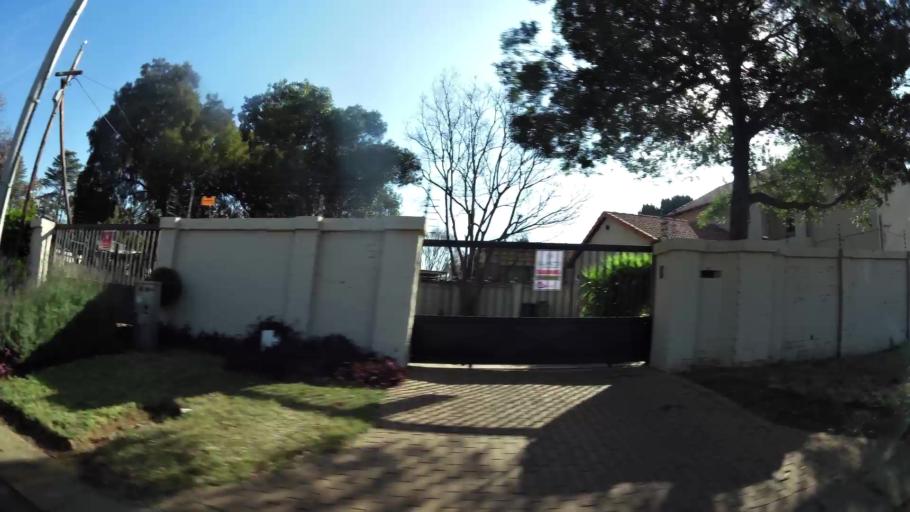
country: ZA
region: Gauteng
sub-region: City of Tshwane Metropolitan Municipality
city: Pretoria
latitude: -25.7259
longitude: 28.2618
